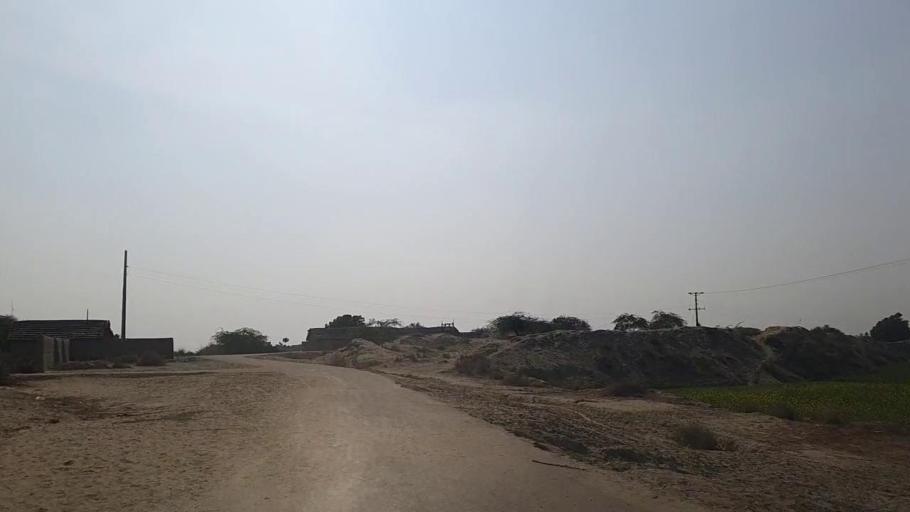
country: PK
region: Sindh
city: Daur
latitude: 26.4609
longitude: 68.4645
